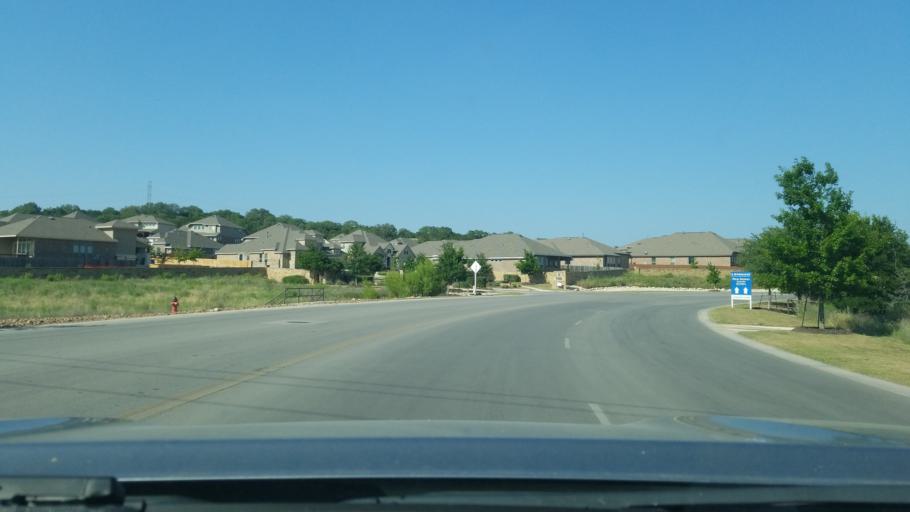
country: US
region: Texas
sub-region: Comal County
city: Bulverde
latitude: 29.7712
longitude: -98.4180
